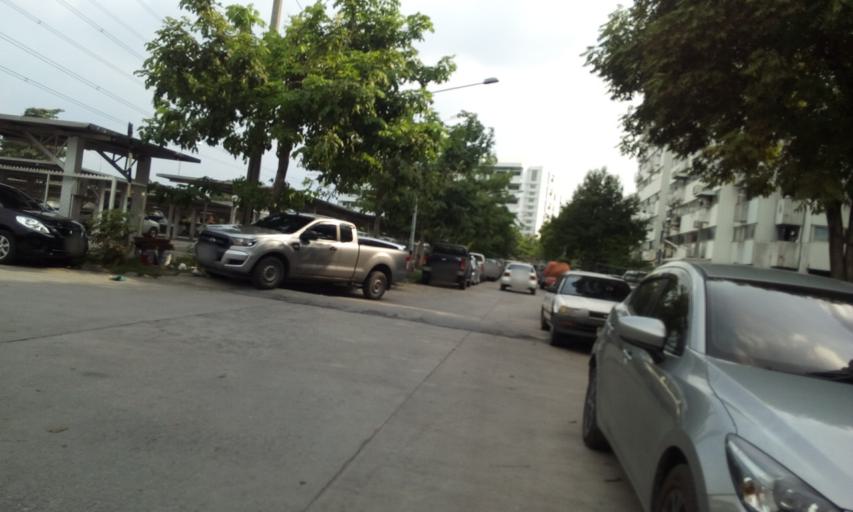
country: TH
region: Bangkok
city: Don Mueang
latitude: 13.9149
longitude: 100.5571
